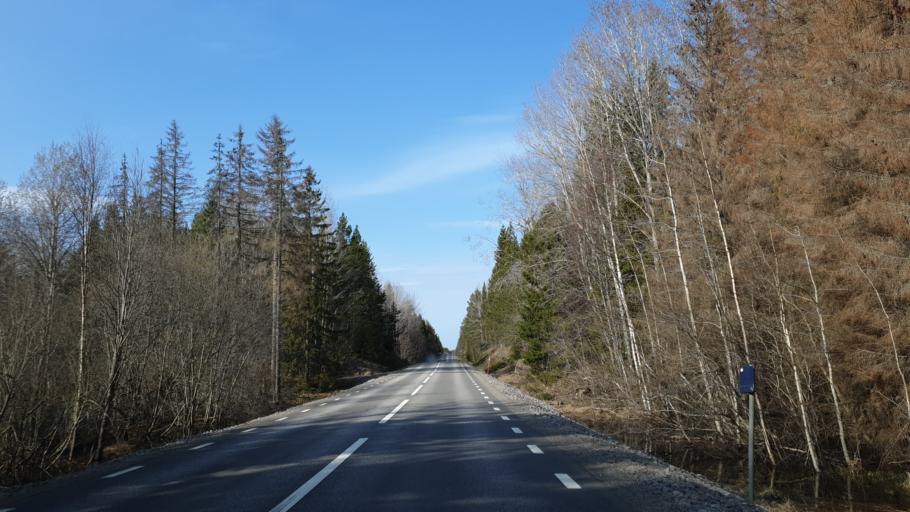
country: SE
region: Gaevleborg
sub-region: Gavle Kommun
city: Norrsundet
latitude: 61.0540
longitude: 17.1424
